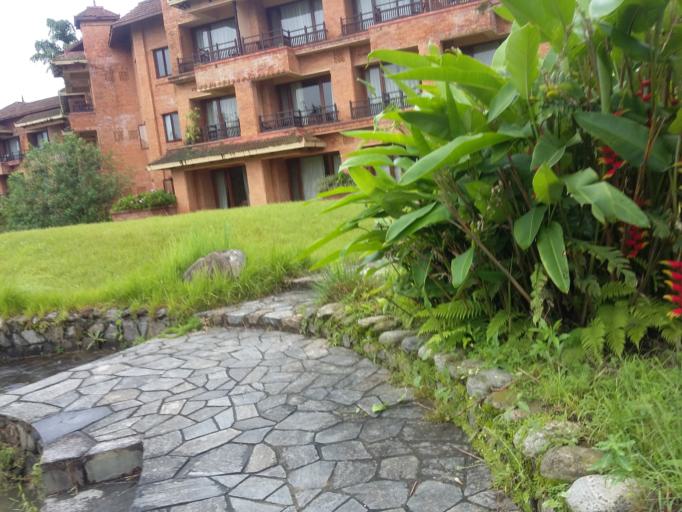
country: NP
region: Western Region
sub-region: Gandaki Zone
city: Pokhara
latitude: 28.1774
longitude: 83.9998
